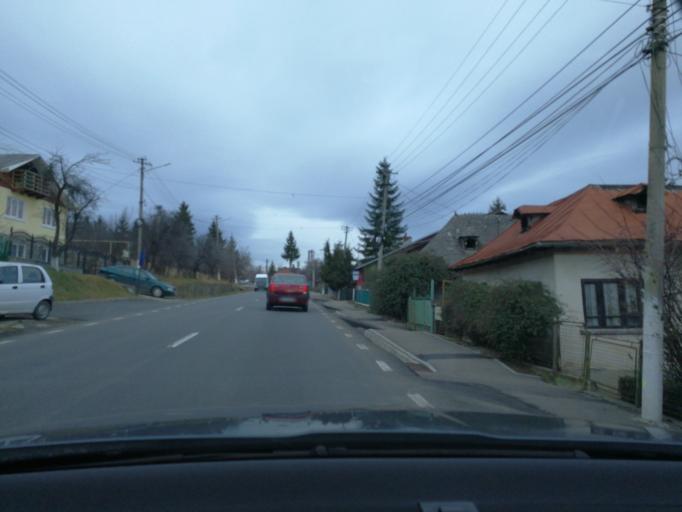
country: RO
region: Prahova
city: Cornu de Sus
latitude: 45.1589
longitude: 25.6865
